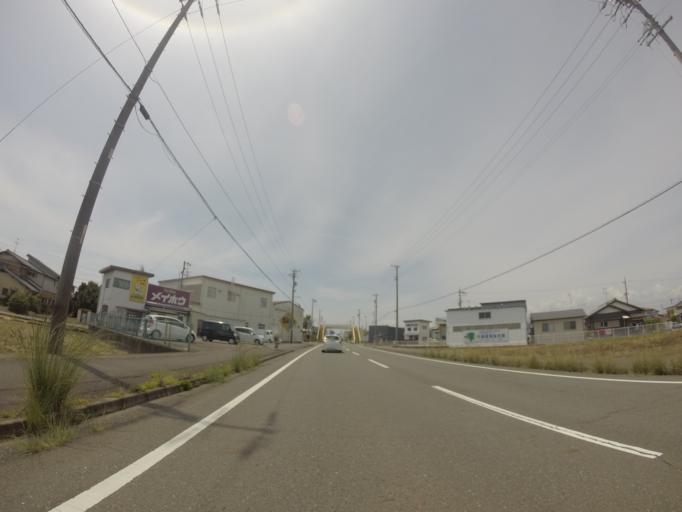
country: JP
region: Shizuoka
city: Yaizu
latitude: 34.8319
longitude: 138.3037
